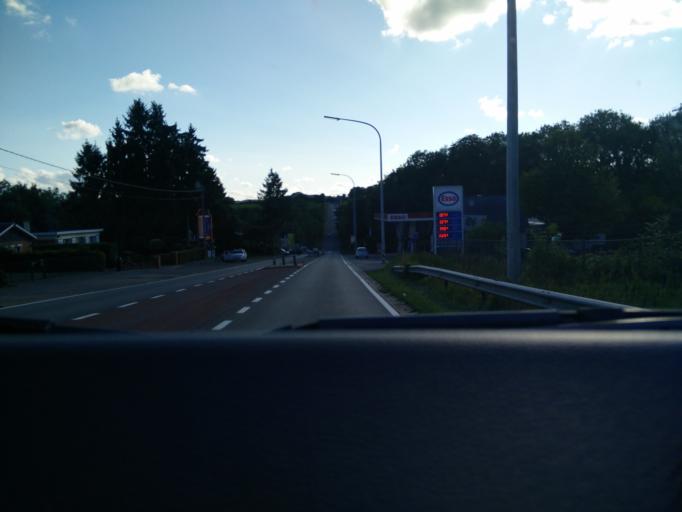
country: BE
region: Wallonia
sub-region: Province du Hainaut
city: Beaumont
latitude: 50.2310
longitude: 4.2360
